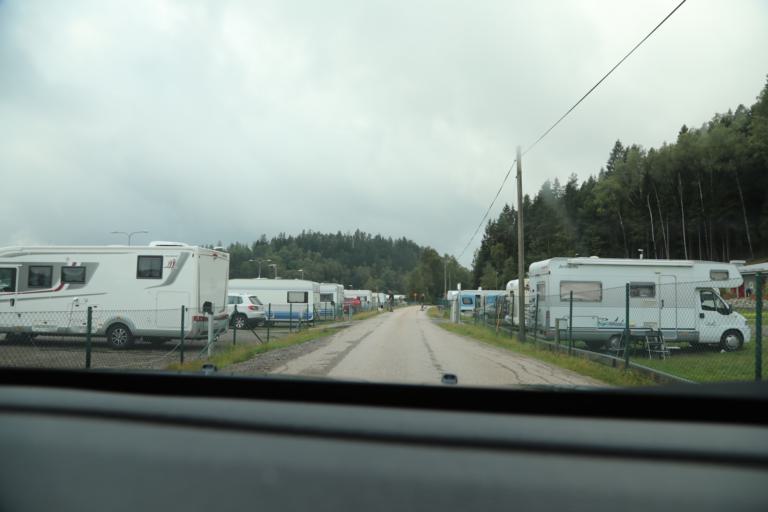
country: SE
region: Halland
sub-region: Falkenbergs Kommun
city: Falkenberg
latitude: 57.1251
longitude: 12.7069
